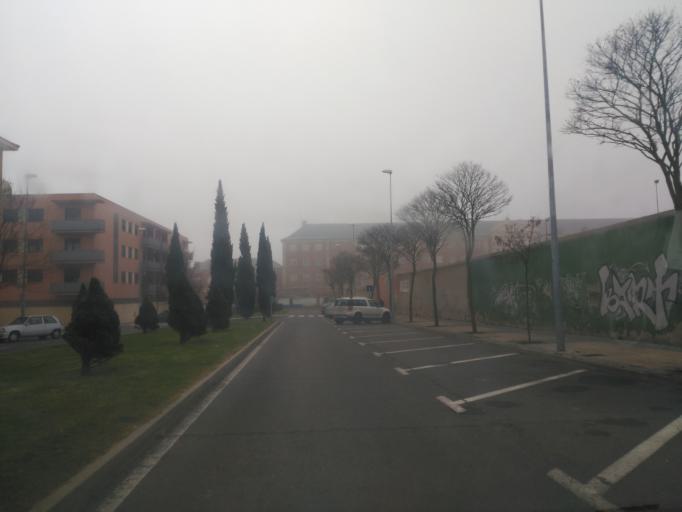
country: ES
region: Castille and Leon
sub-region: Provincia de Salamanca
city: Salamanca
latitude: 40.9703
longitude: -5.6412
